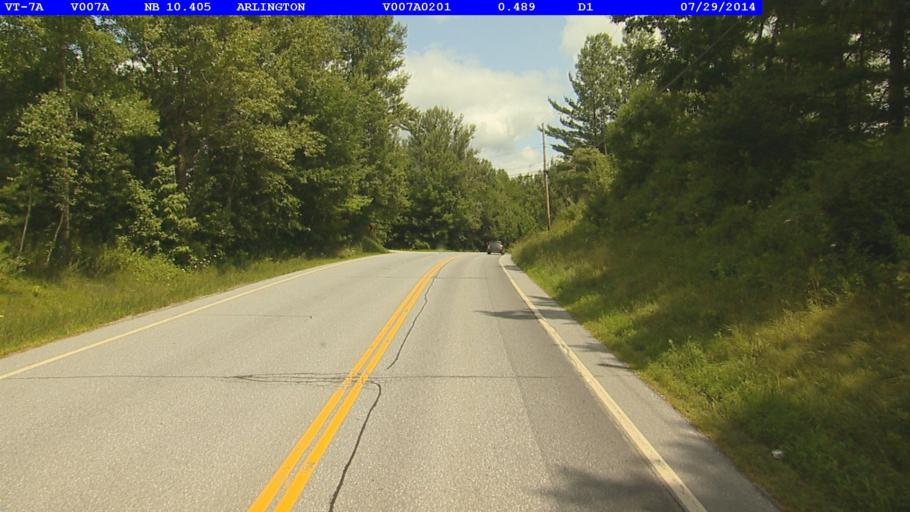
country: US
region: Vermont
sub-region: Bennington County
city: Arlington
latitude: 43.0335
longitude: -73.1823
